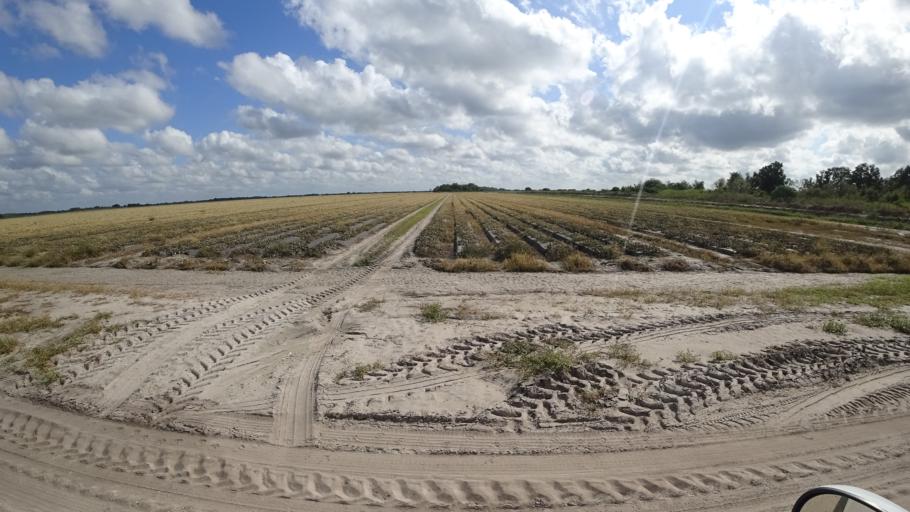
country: US
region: Florida
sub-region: Sarasota County
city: Lake Sarasota
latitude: 27.4300
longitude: -82.1826
